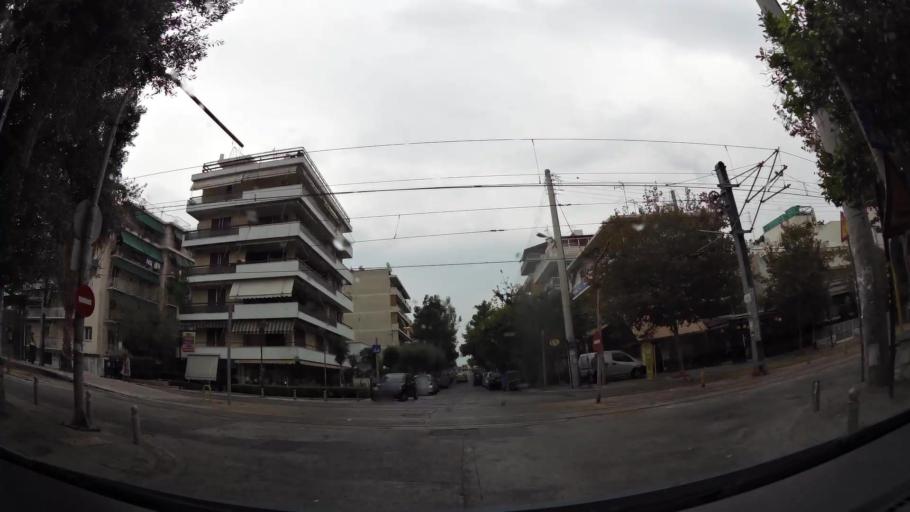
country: GR
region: Attica
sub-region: Nomarchia Athinas
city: Palaio Faliro
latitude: 37.9249
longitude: 23.7015
